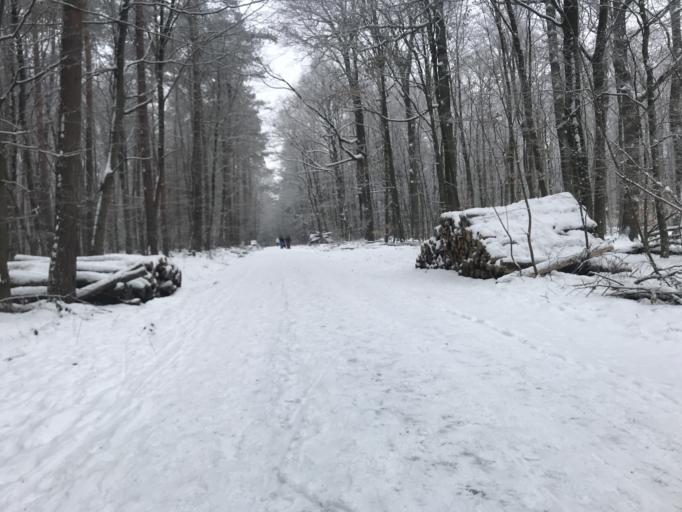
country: DE
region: Hesse
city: Eppstein
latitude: 50.1153
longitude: 8.3933
